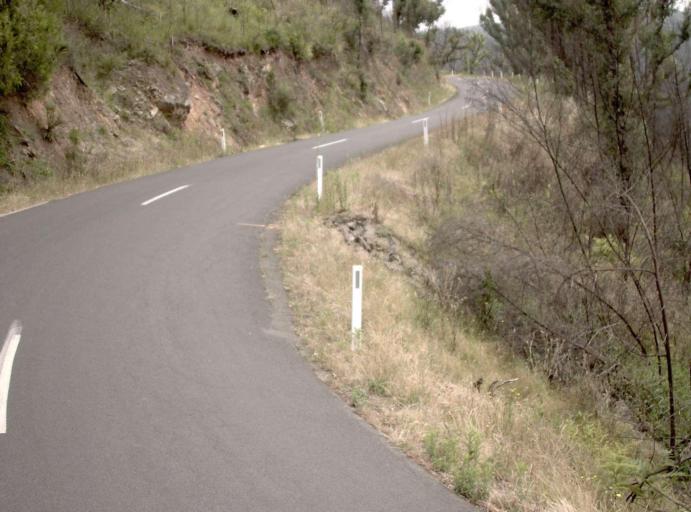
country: AU
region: Victoria
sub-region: Wellington
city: Heyfield
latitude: -37.7315
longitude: 146.6697
